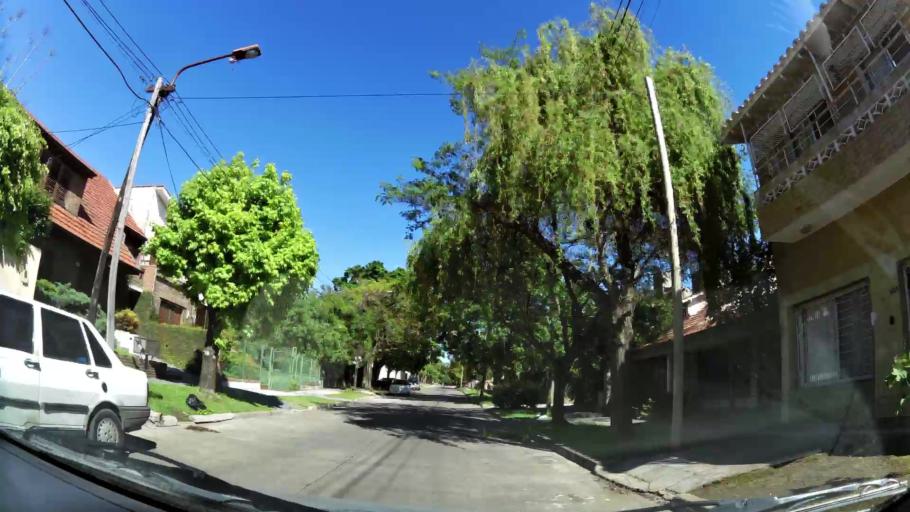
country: AR
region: Buenos Aires
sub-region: Partido de Quilmes
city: Quilmes
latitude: -34.7006
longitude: -58.2909
